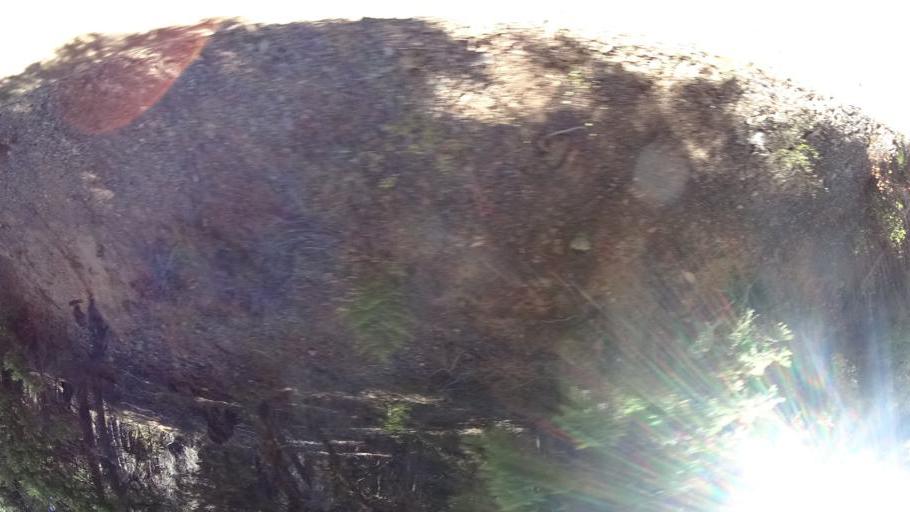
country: US
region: California
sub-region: Siskiyou County
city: Happy Camp
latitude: 41.3284
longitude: -123.0503
